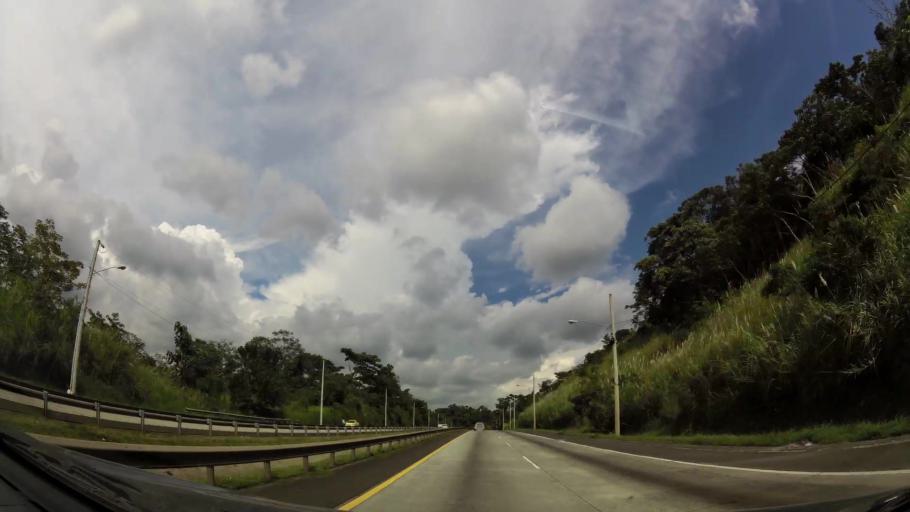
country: PA
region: Panama
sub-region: Distrito de Panama
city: Paraiso
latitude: 9.0382
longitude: -79.5730
